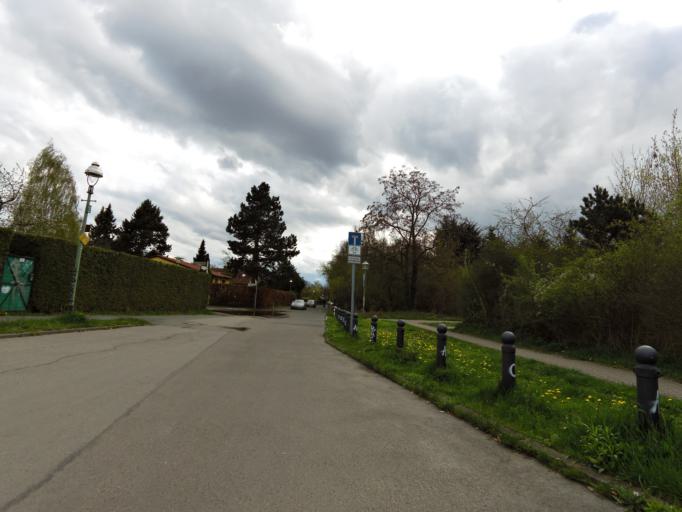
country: DE
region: Berlin
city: Lichtenrade
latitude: 52.4008
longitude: 13.3899
